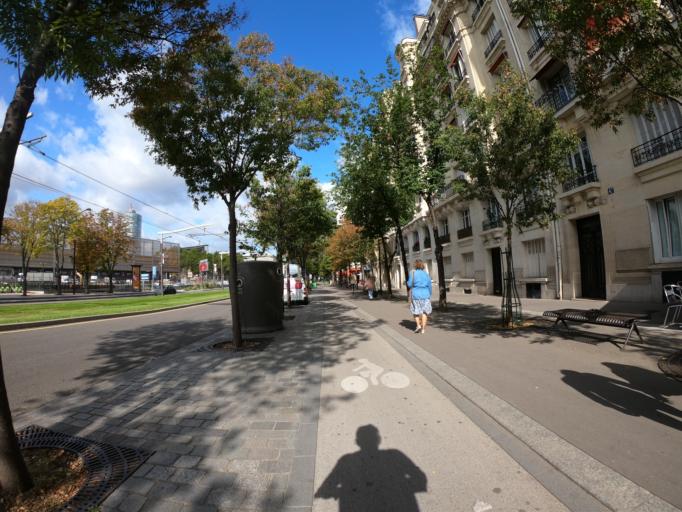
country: FR
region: Ile-de-France
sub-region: Departement des Hauts-de-Seine
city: Vanves
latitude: 48.8337
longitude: 2.2862
